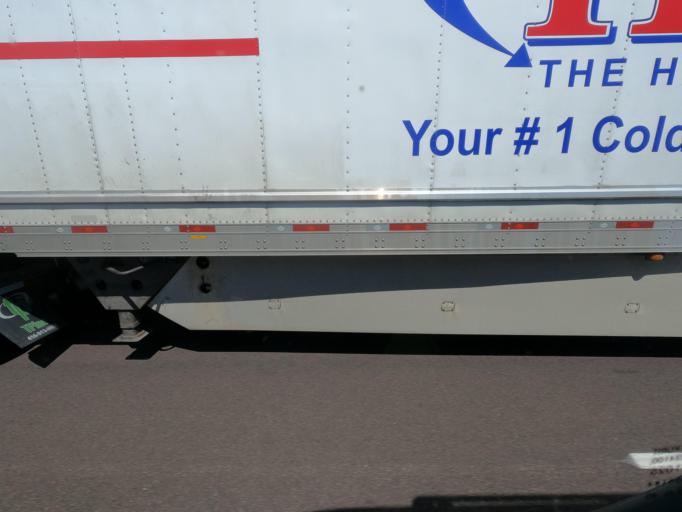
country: US
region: Wyoming
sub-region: Albany County
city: Laramie
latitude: 41.4334
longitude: -105.8930
